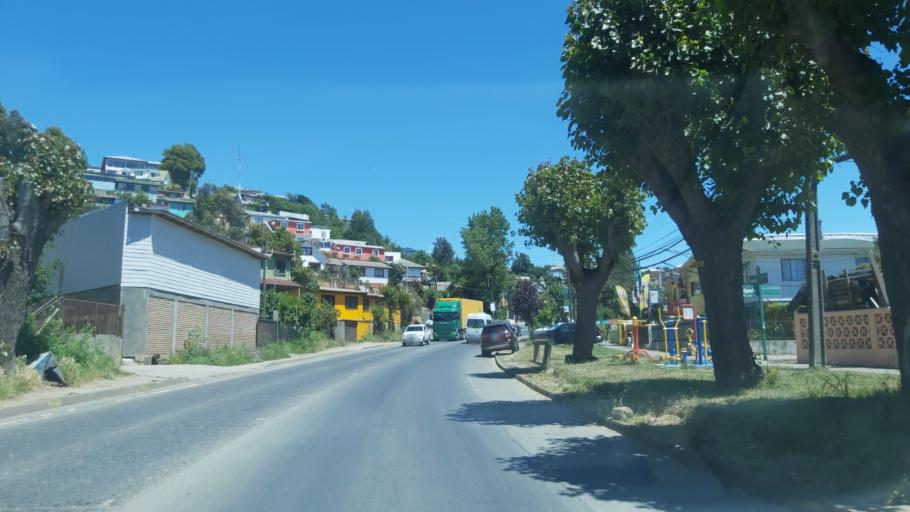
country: CL
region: Maule
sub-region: Provincia de Talca
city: Constitucion
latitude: -35.3340
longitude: -72.4163
